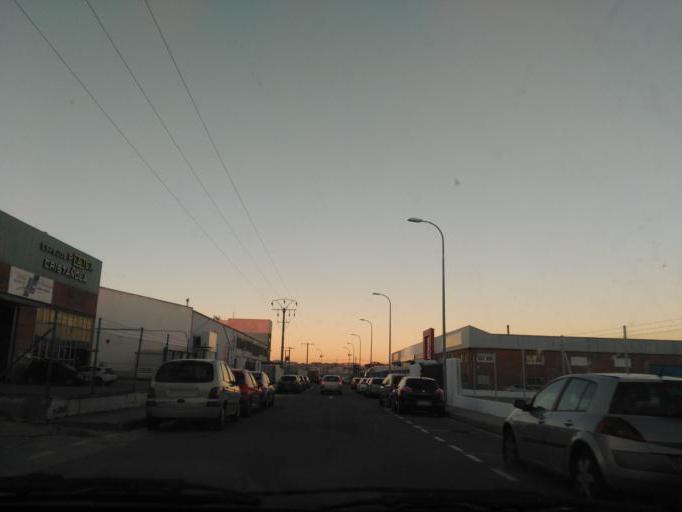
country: ES
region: Castille and Leon
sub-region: Provincia de Salamanca
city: Carbajosa de la Sagrada
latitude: 40.9461
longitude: -5.6528
